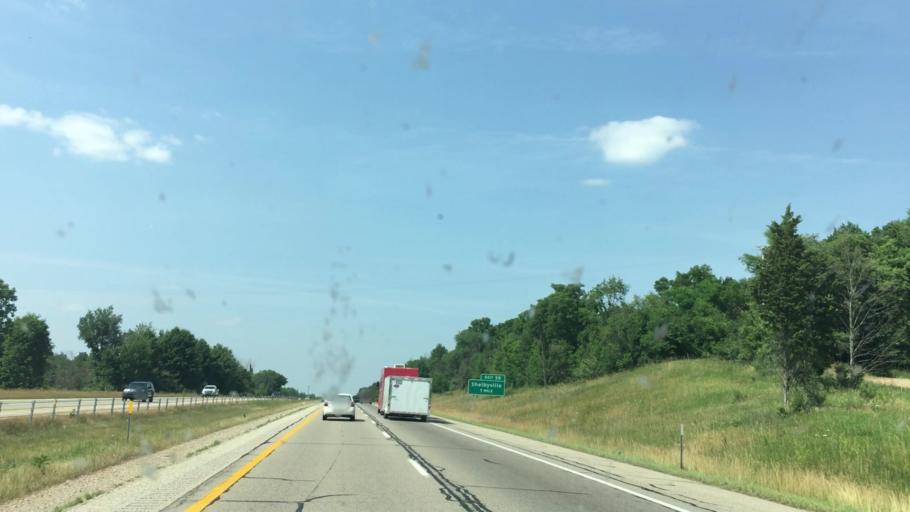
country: US
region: Michigan
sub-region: Allegan County
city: Wayland
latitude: 42.5749
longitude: -85.6624
